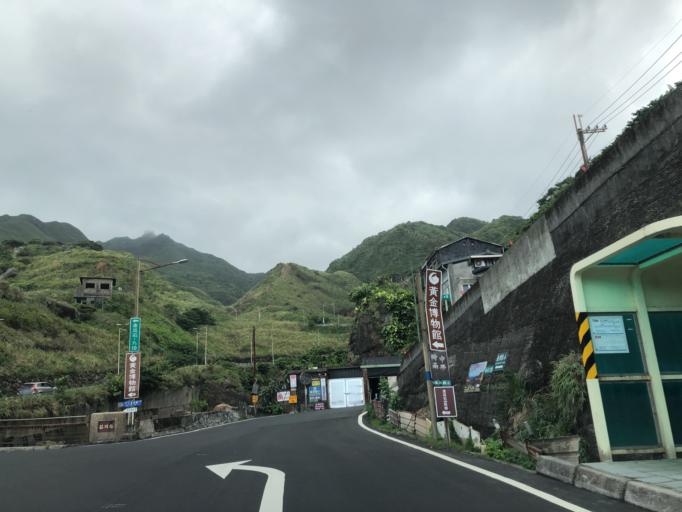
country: TW
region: Taiwan
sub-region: Keelung
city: Keelung
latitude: 25.1200
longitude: 121.8618
